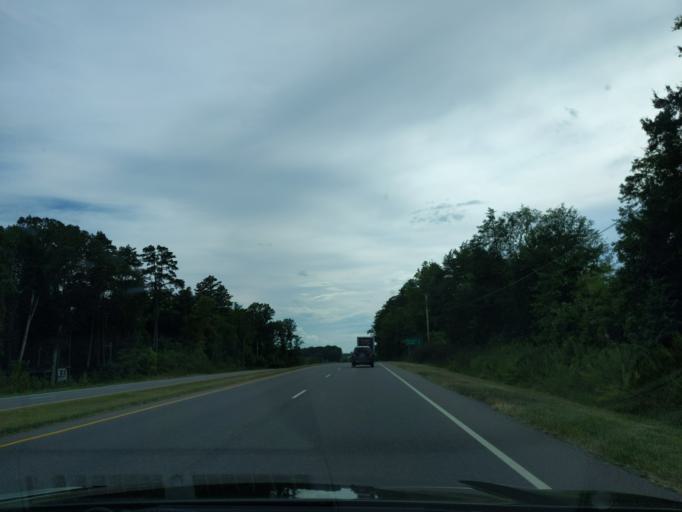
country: US
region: North Carolina
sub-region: Cabarrus County
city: Mount Pleasant
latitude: 35.4013
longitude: -80.4659
